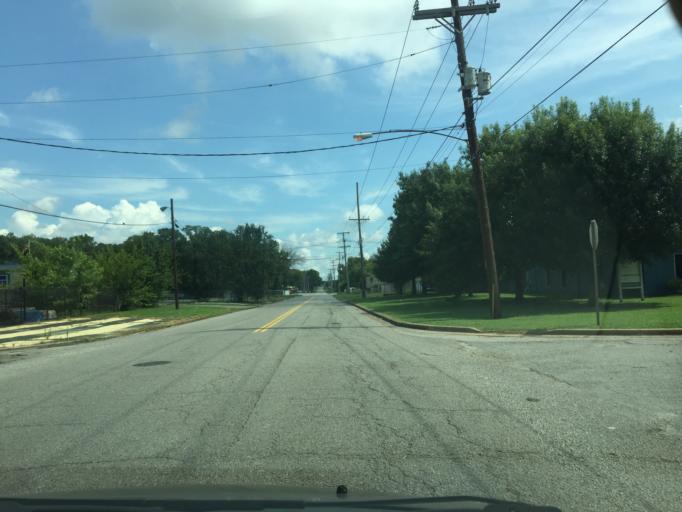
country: US
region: Tennessee
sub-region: Hamilton County
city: East Chattanooga
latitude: 35.0758
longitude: -85.2539
